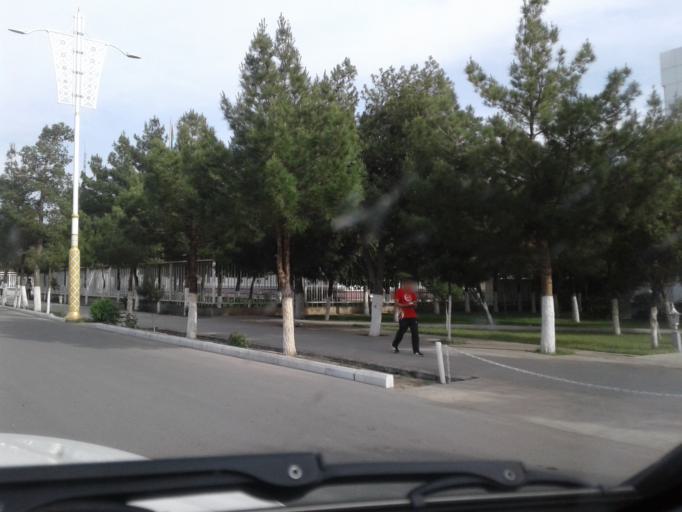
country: TM
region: Mary
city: Mary
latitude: 37.5938
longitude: 61.8389
